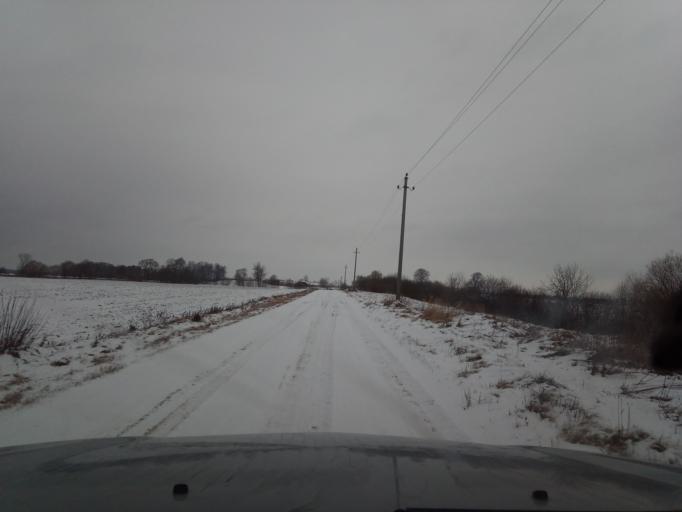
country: LT
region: Vilnius County
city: Ukmerge
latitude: 55.4782
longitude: 24.6282
